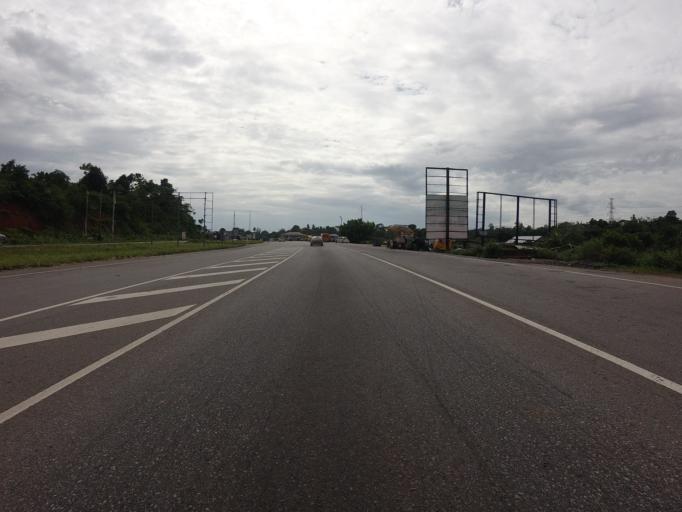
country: GH
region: Eastern
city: Nkawkaw
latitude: 6.5967
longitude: -0.8328
